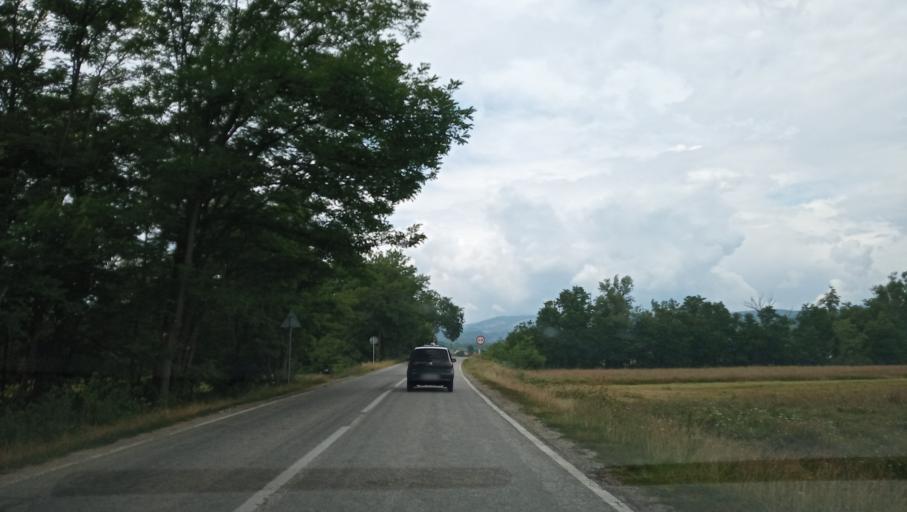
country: RO
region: Gorj
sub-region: Comuna Tismana
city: Tismana
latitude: 45.0375
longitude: 22.9639
